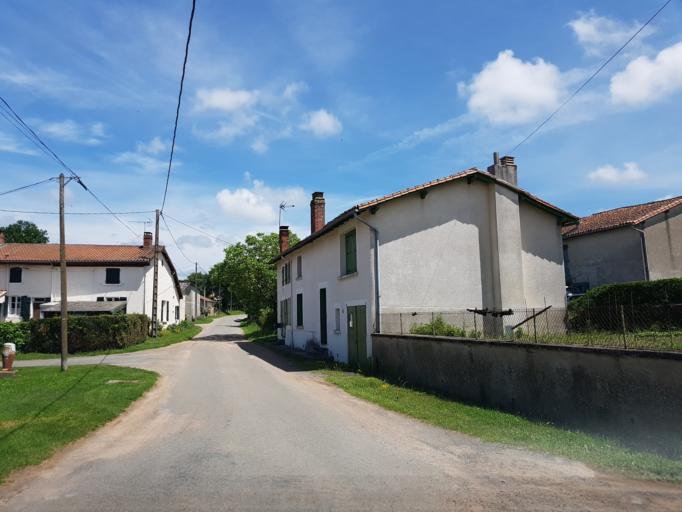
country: FR
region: Poitou-Charentes
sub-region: Departement de la Charente
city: Etagnac
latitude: 45.9035
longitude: 0.7515
